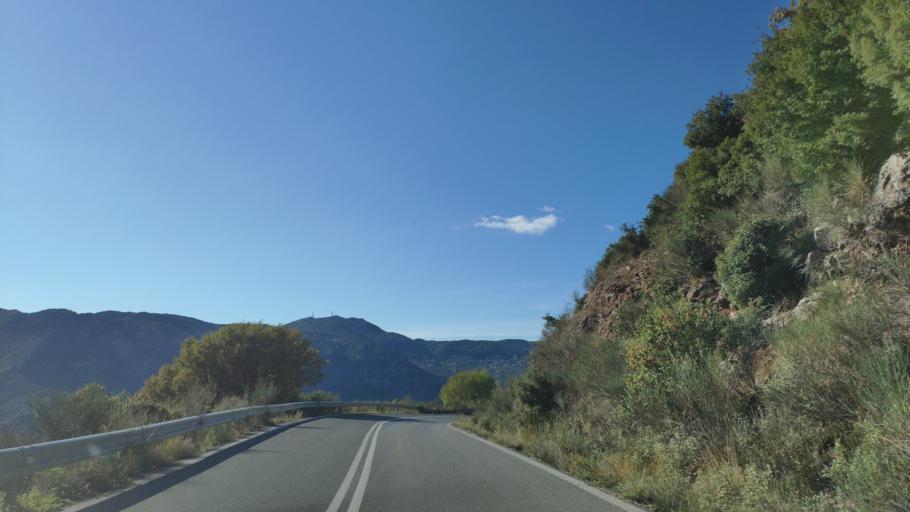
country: GR
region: Peloponnese
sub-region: Nomos Arkadias
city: Dimitsana
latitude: 37.5761
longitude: 22.0611
